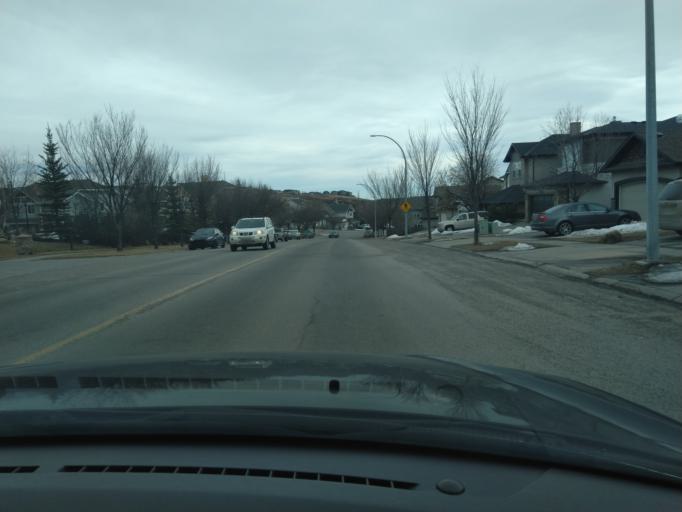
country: CA
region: Alberta
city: Calgary
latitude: 51.1613
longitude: -114.1019
